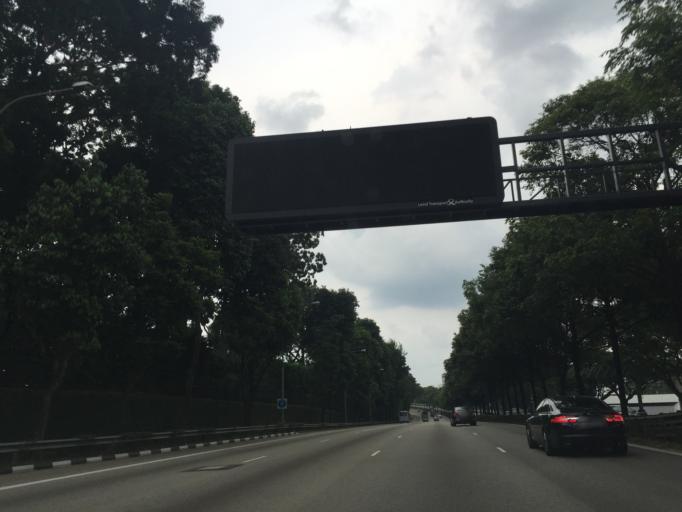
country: SG
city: Singapore
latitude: 1.3260
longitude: 103.7405
